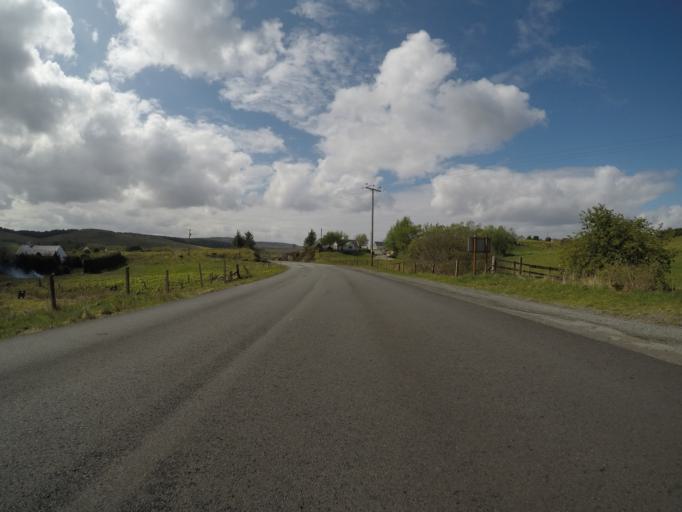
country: GB
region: Scotland
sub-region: Highland
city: Isle of Skye
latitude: 57.4534
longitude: -6.2952
